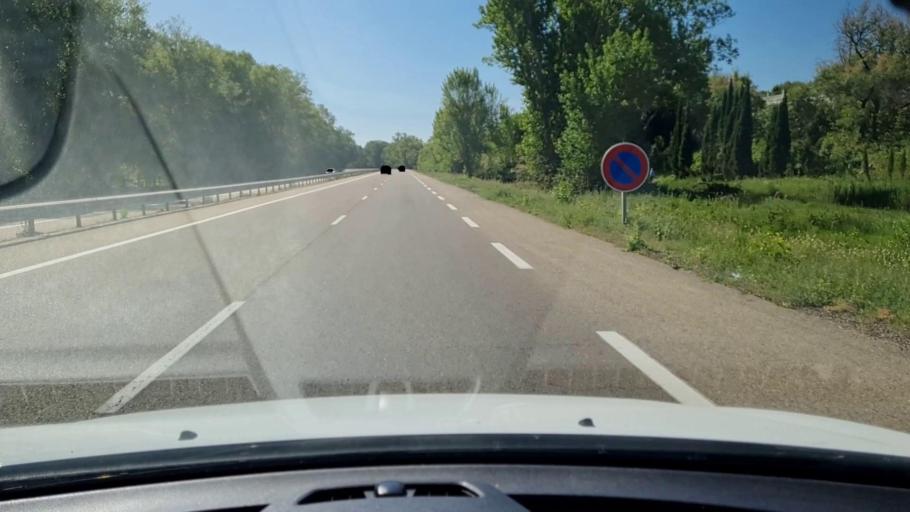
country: FR
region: Languedoc-Roussillon
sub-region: Departement de l'Herault
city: La Grande-Motte
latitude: 43.5725
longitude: 4.1060
